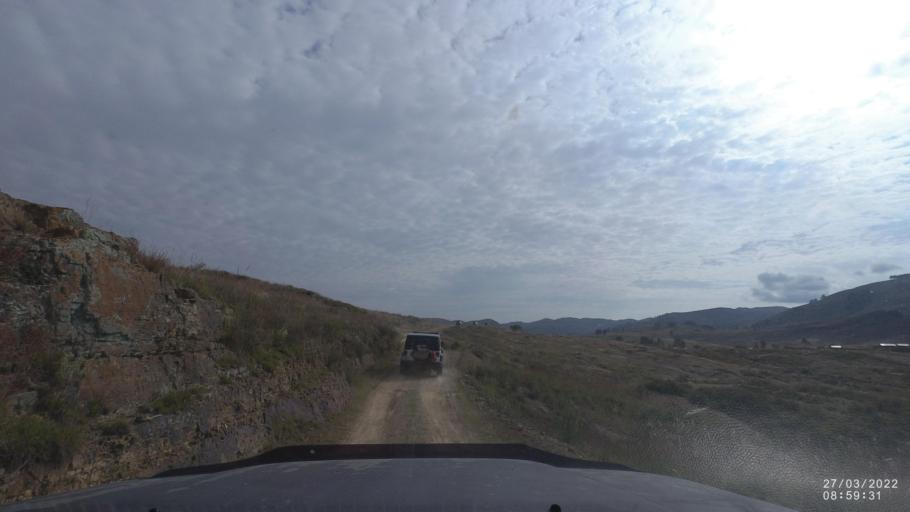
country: BO
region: Cochabamba
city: Cliza
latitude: -17.7391
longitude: -65.8544
